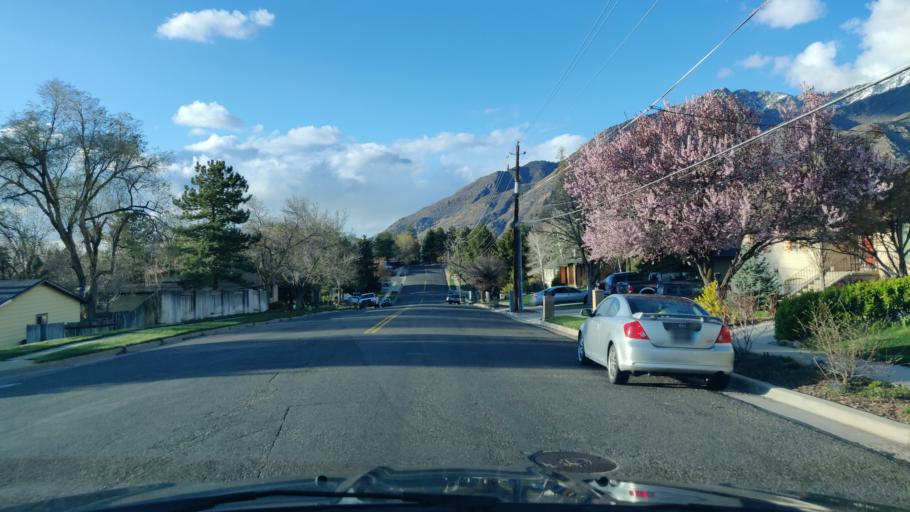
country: US
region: Utah
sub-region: Salt Lake County
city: Cottonwood Heights
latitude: 40.6132
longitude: -111.7960
